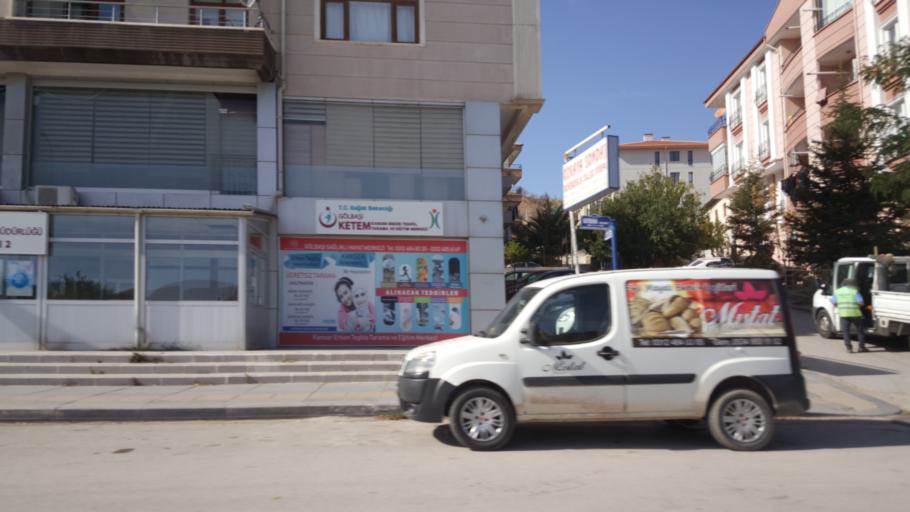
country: TR
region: Ankara
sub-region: Goelbasi
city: Golbasi
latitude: 39.8017
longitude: 32.7988
